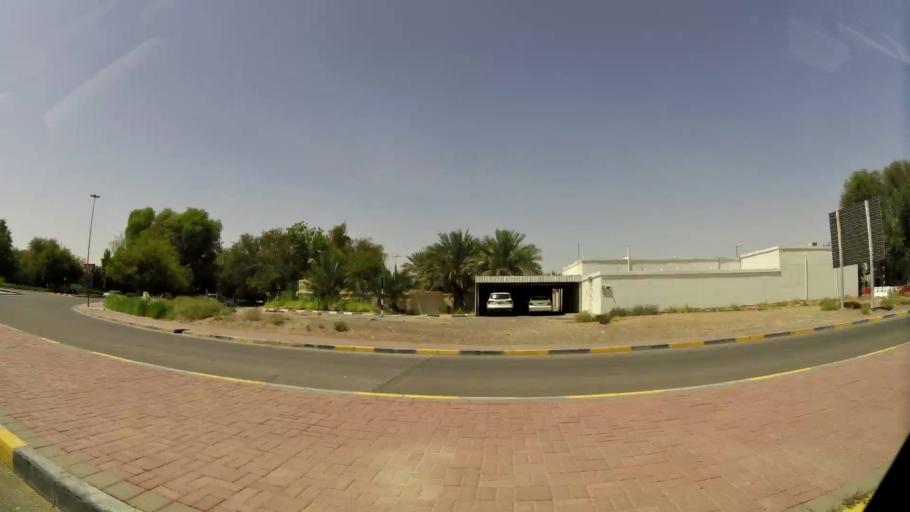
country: OM
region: Al Buraimi
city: Al Buraymi
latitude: 24.2833
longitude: 55.7650
